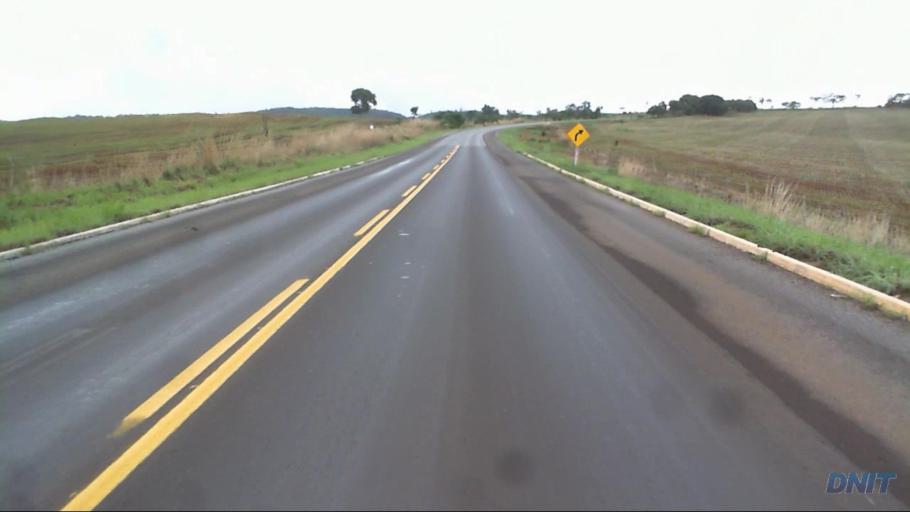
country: BR
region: Goias
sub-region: Padre Bernardo
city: Padre Bernardo
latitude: -15.2107
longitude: -48.4864
